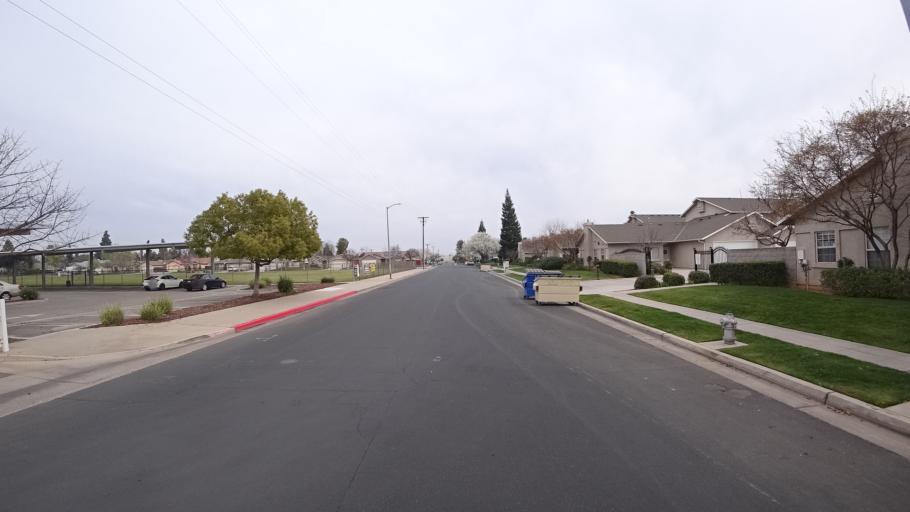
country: US
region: California
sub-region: Fresno County
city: Fresno
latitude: 36.8410
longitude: -119.8151
